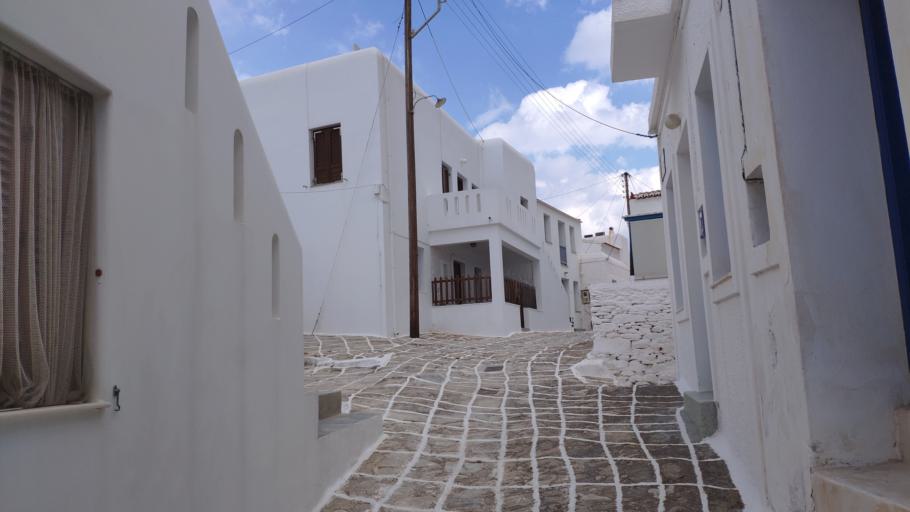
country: GR
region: South Aegean
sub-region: Nomos Kykladon
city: Kythnos
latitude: 37.4121
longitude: 24.4307
